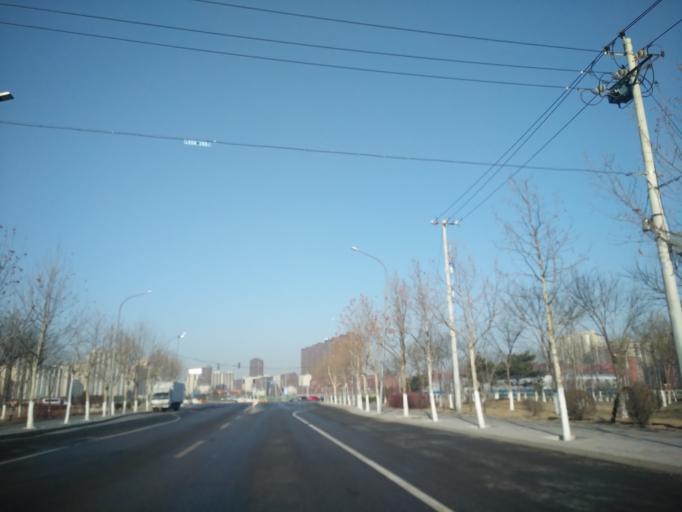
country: CN
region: Beijing
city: Yinghai
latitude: 39.7507
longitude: 116.4908
